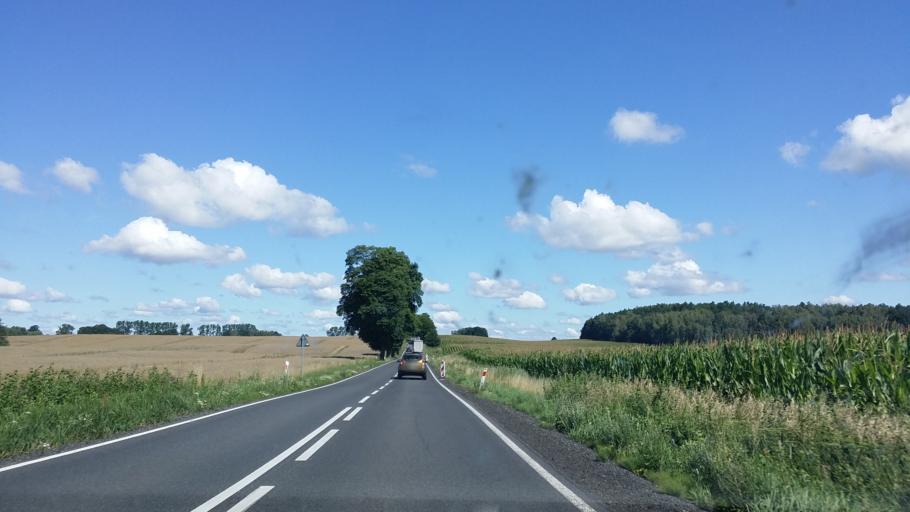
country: PL
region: West Pomeranian Voivodeship
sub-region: Powiat drawski
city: Kalisz Pomorski
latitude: 53.3148
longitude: 15.9072
